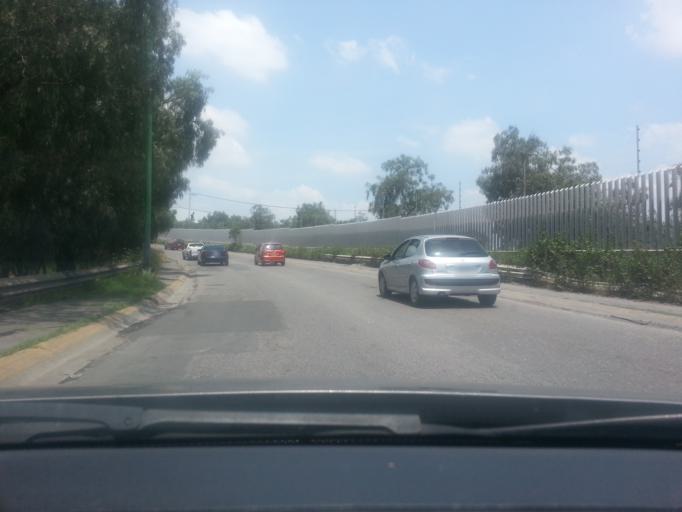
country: MX
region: Mexico
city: Cuautitlan
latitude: 19.6554
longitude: -99.1957
